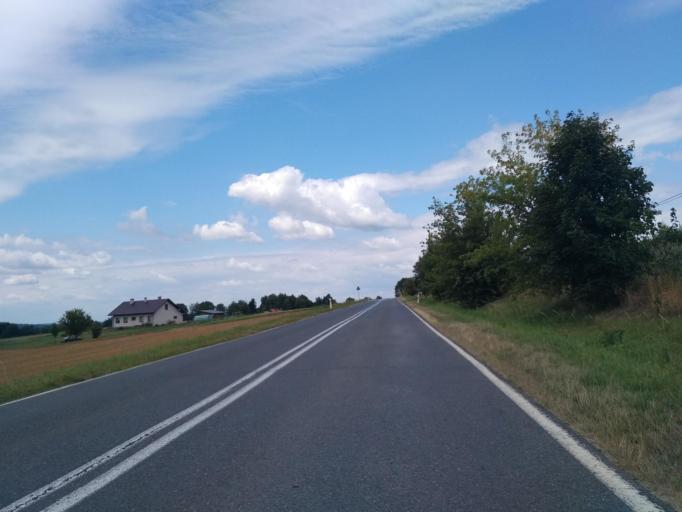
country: PL
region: Subcarpathian Voivodeship
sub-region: Powiat rzeszowski
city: Hyzne
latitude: 49.8941
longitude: 22.2306
